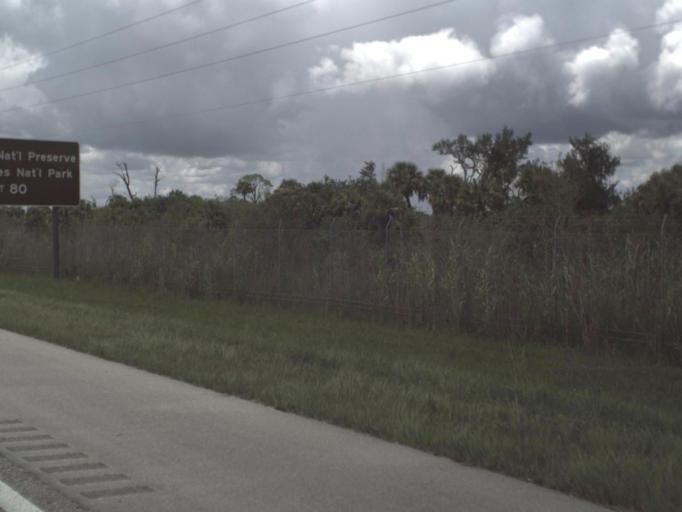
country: US
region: Florida
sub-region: Collier County
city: Immokalee
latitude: 26.1551
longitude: -81.3258
